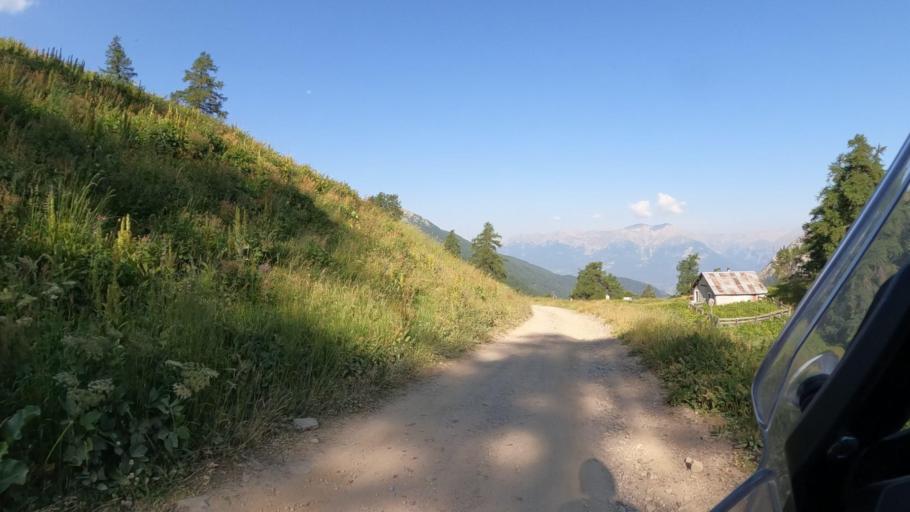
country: FR
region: Provence-Alpes-Cote d'Azur
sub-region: Departement des Hautes-Alpes
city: Guillestre
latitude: 44.5896
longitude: 6.6255
